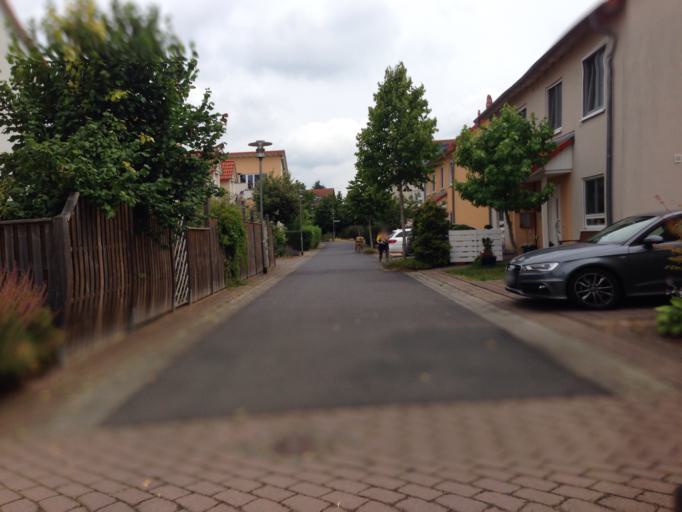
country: DE
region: Hesse
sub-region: Regierungsbezirk Darmstadt
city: Grosskrotzenburg
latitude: 50.1015
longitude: 8.9516
